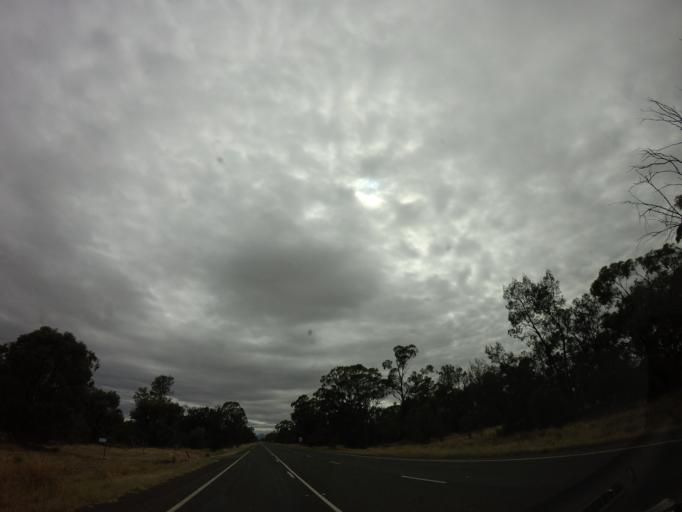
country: AU
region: New South Wales
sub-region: Narrabri
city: Narrabri
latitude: -30.3529
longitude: 149.7500
